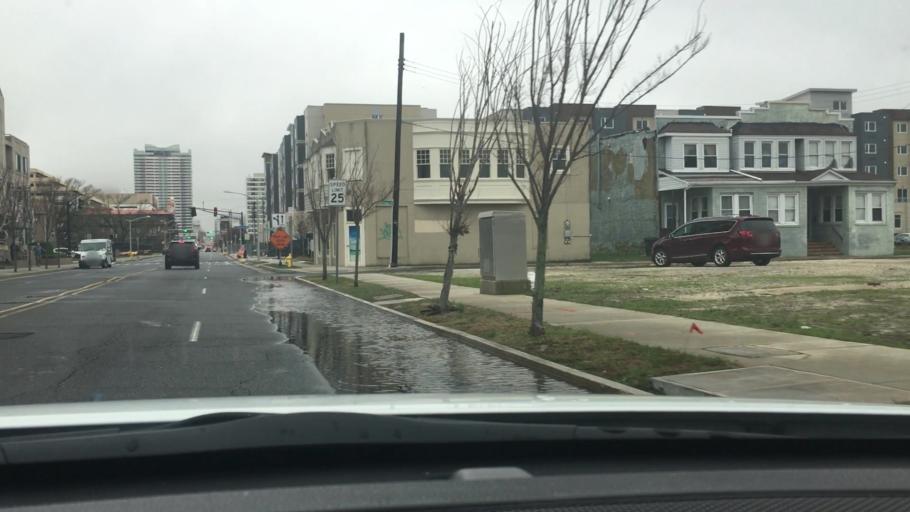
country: US
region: New Jersey
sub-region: Atlantic County
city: Atlantic City
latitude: 39.3651
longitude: -74.4161
